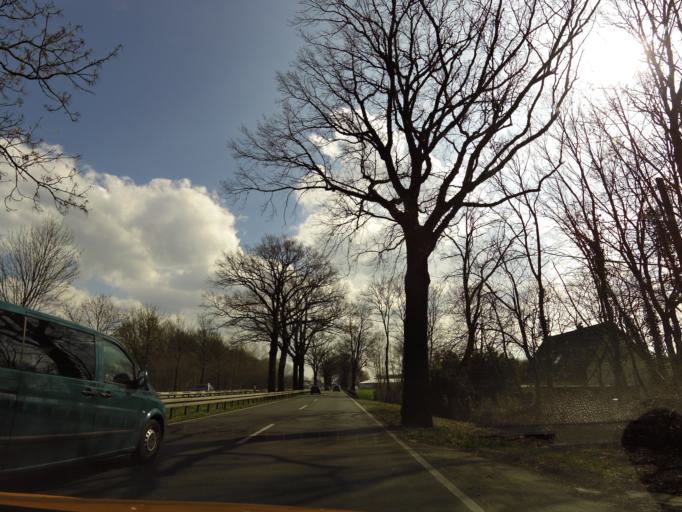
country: DE
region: Brandenburg
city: Schoneiche
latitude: 52.5006
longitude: 13.7257
